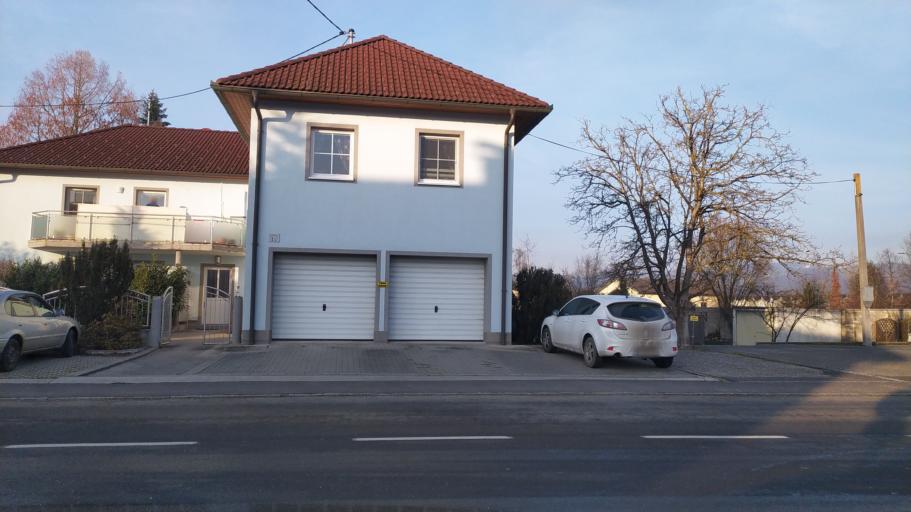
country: AT
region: Upper Austria
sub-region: Politischer Bezirk Urfahr-Umgebung
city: Feldkirchen an der Donau
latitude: 48.3460
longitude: 14.0546
